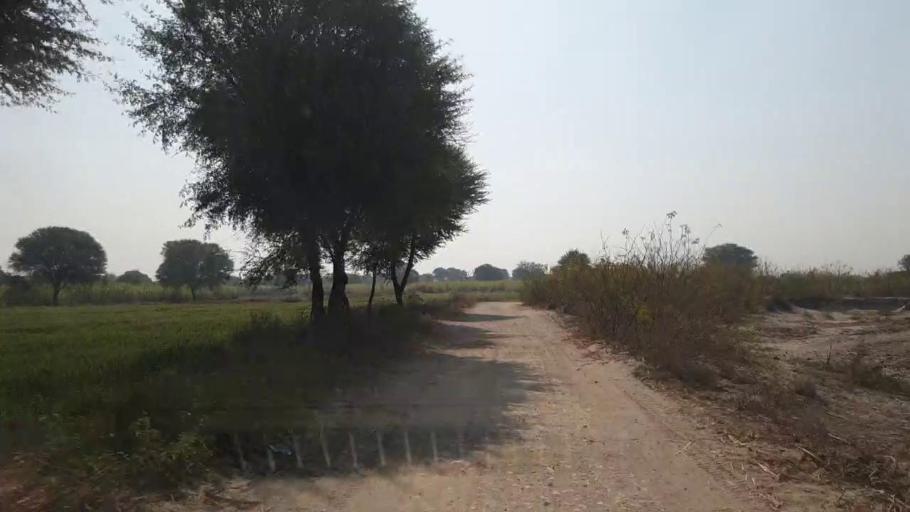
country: PK
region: Sindh
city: Tando Jam
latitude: 25.3275
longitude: 68.6101
